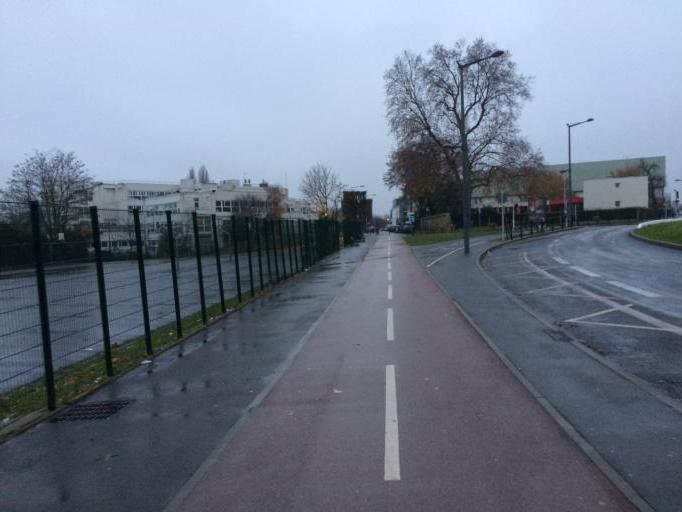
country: FR
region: Ile-de-France
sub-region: Departement de l'Essonne
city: Athis-Mons
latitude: 48.7132
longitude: 2.3965
